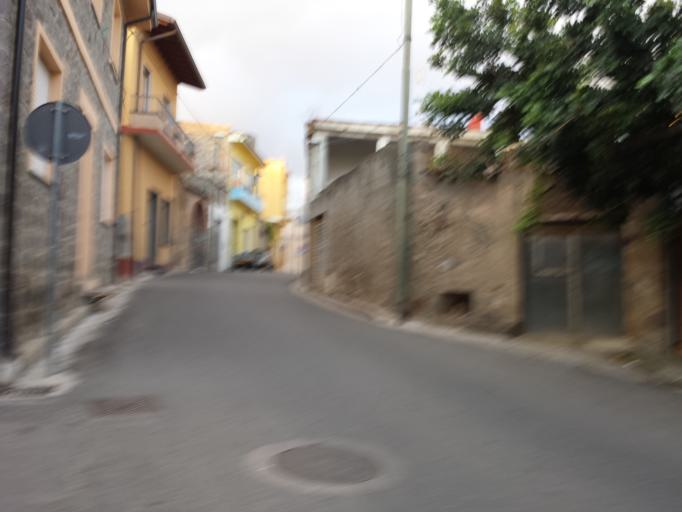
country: IT
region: Sardinia
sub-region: Provincia di Medio Campidano
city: Serrenti
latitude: 39.4939
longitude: 8.9758
